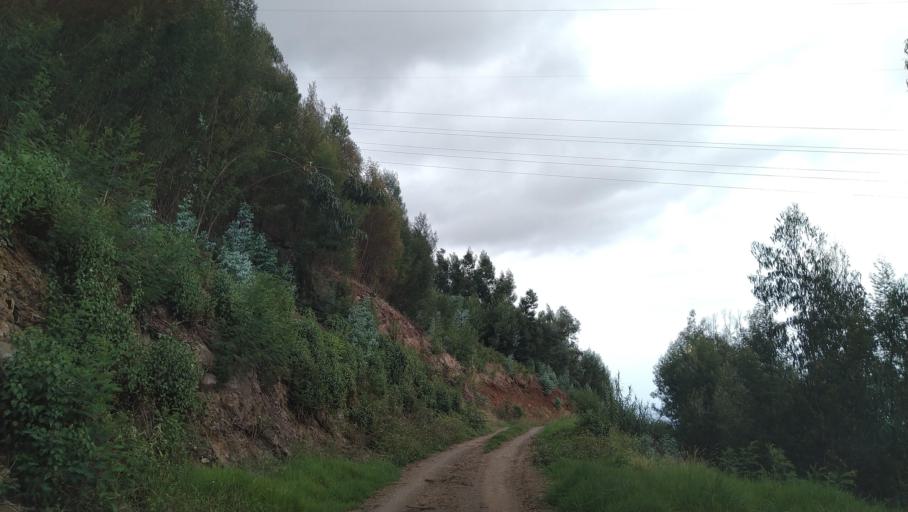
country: PT
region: Madeira
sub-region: Funchal
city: Nossa Senhora do Monte
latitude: 32.6805
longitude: -16.9232
